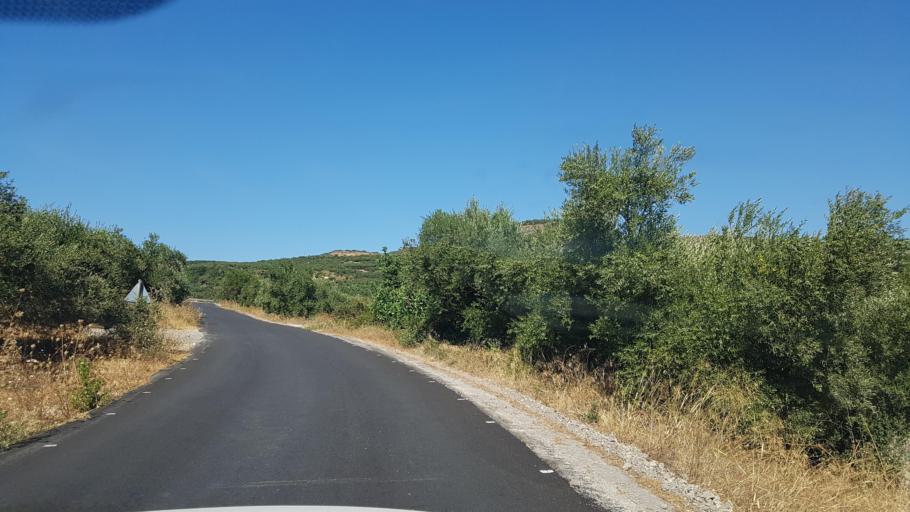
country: GR
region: Crete
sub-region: Nomos Chanias
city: Kissamos
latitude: 35.4960
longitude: 23.7212
